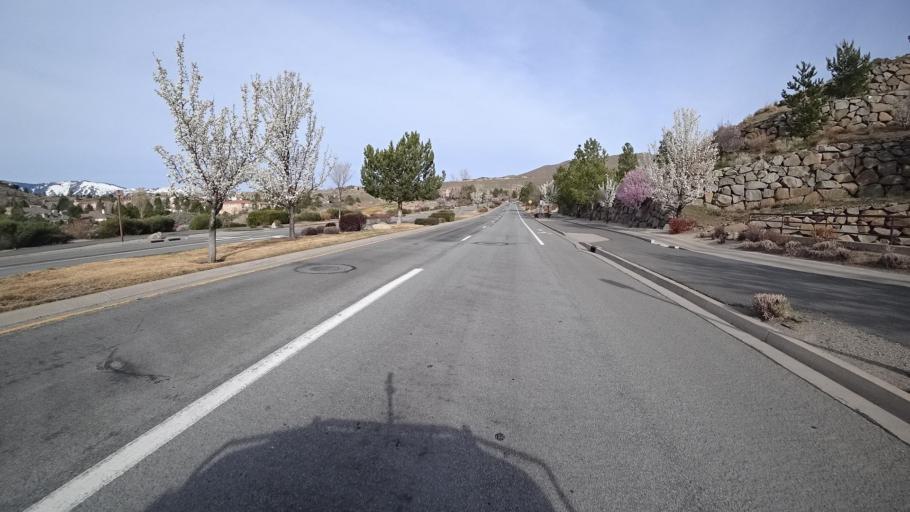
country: US
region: Nevada
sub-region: Washoe County
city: Mogul
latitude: 39.5342
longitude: -119.9212
